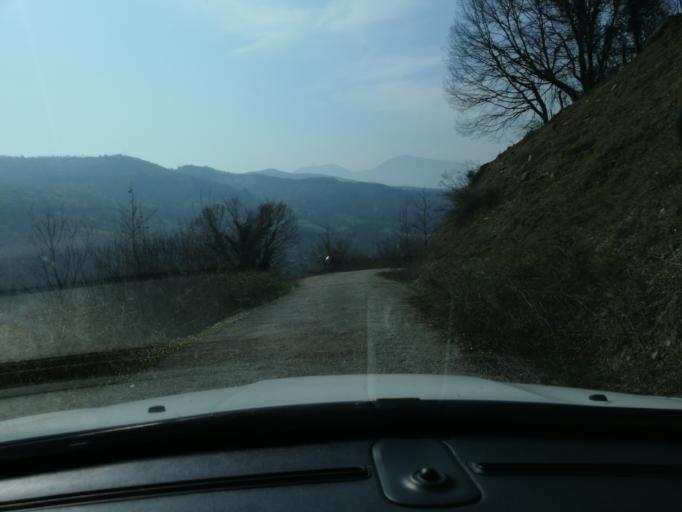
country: TR
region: Karabuk
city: Yenice
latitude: 41.2673
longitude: 32.3600
